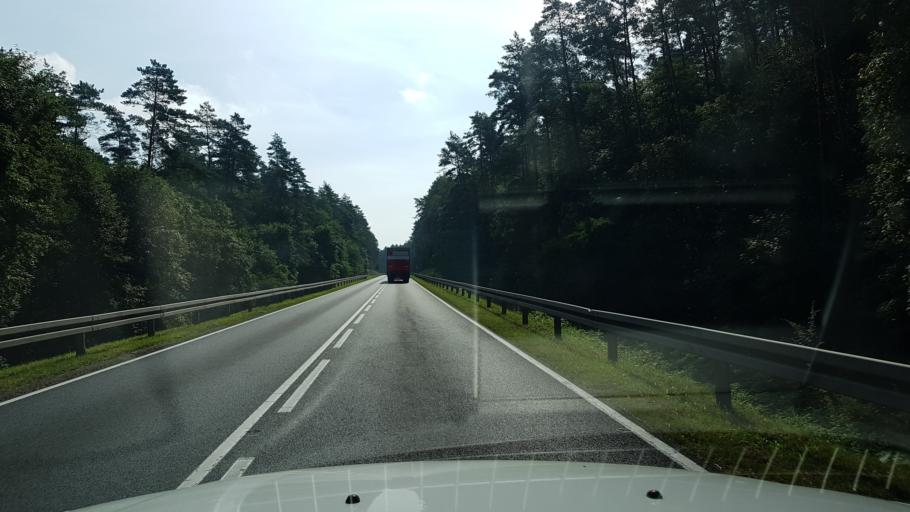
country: PL
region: West Pomeranian Voivodeship
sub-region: Powiat walecki
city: Miroslawiec
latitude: 53.3495
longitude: 16.1667
